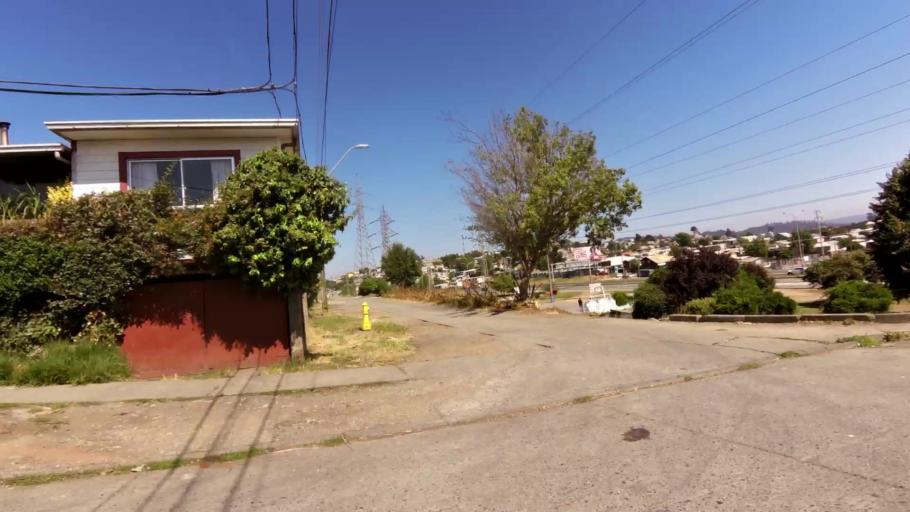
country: CL
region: Biobio
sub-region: Provincia de Concepcion
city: Concepcion
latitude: -36.8036
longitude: -73.0389
